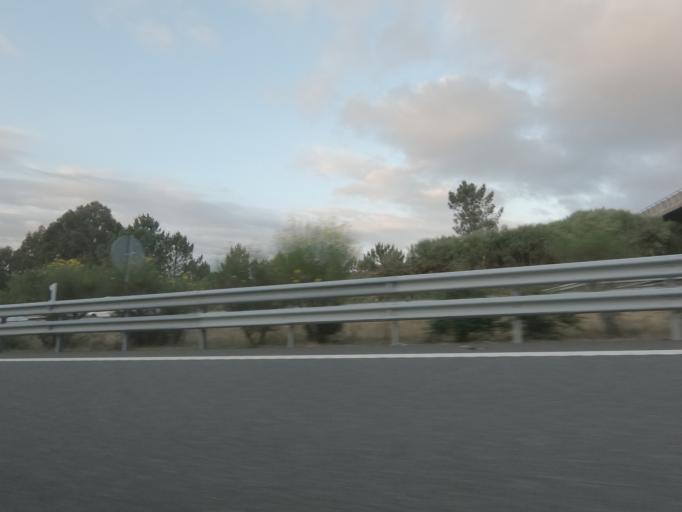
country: ES
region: Galicia
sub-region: Provincia de Pontevedra
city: Covelo
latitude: 42.1913
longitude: -8.3083
